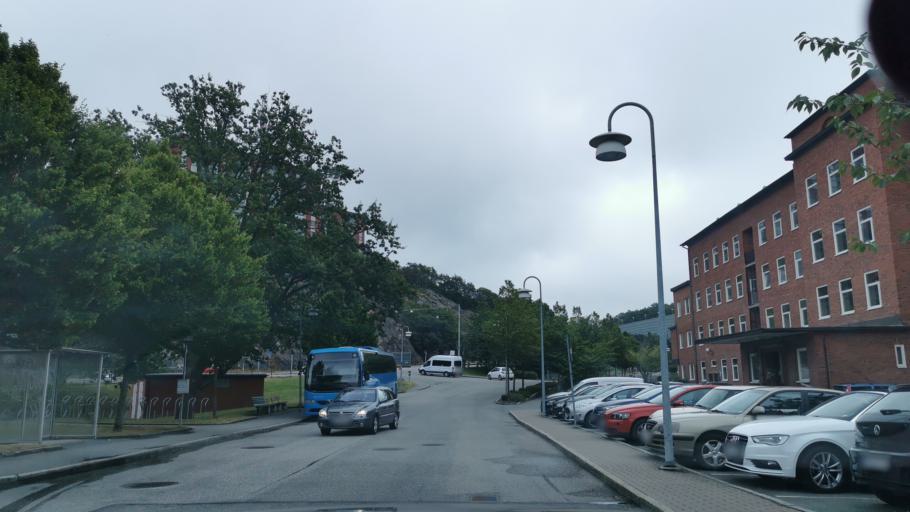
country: SE
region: Vaestra Goetaland
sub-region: Goteborg
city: Goeteborg
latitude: 57.6819
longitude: 11.9636
